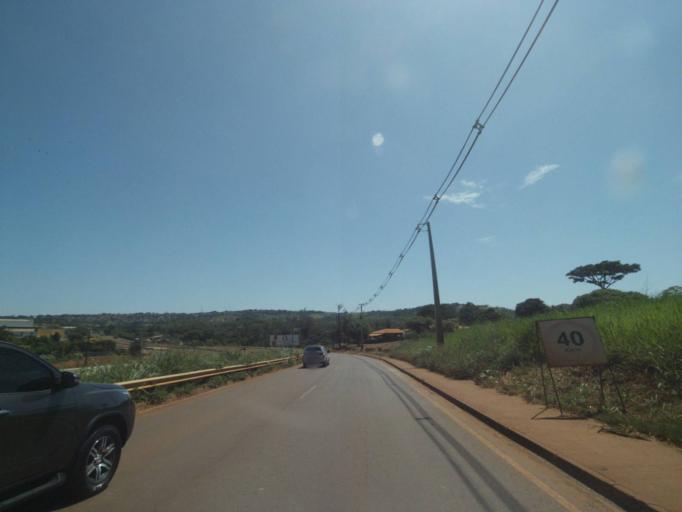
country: BR
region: Parana
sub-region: Londrina
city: Londrina
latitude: -23.4037
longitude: -51.1345
